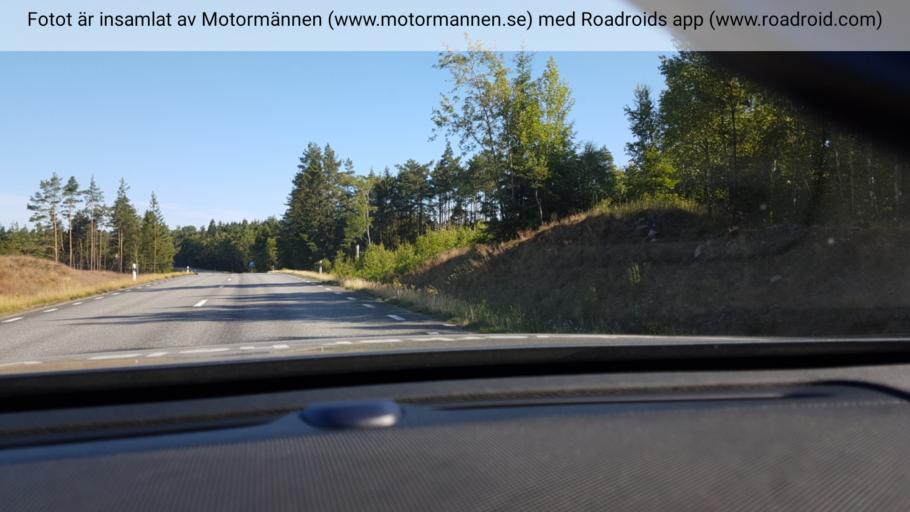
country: SE
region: Kronoberg
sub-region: Markaryds Kommun
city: Markaryd
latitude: 56.4246
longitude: 13.6244
